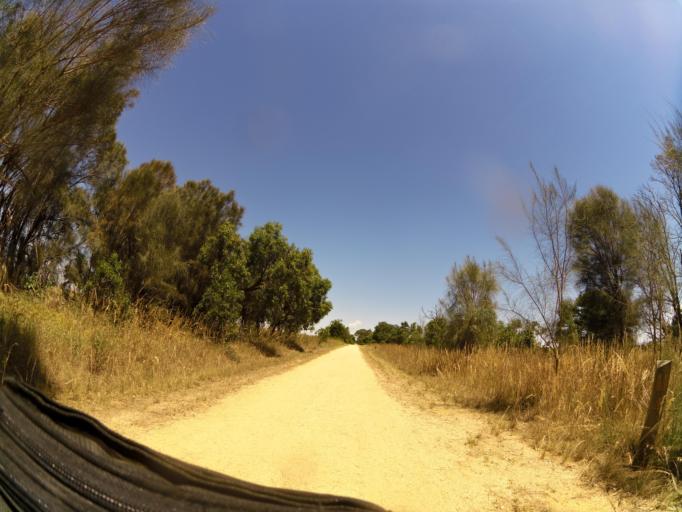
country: AU
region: Victoria
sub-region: Wellington
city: Sale
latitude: -37.9776
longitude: 147.0317
